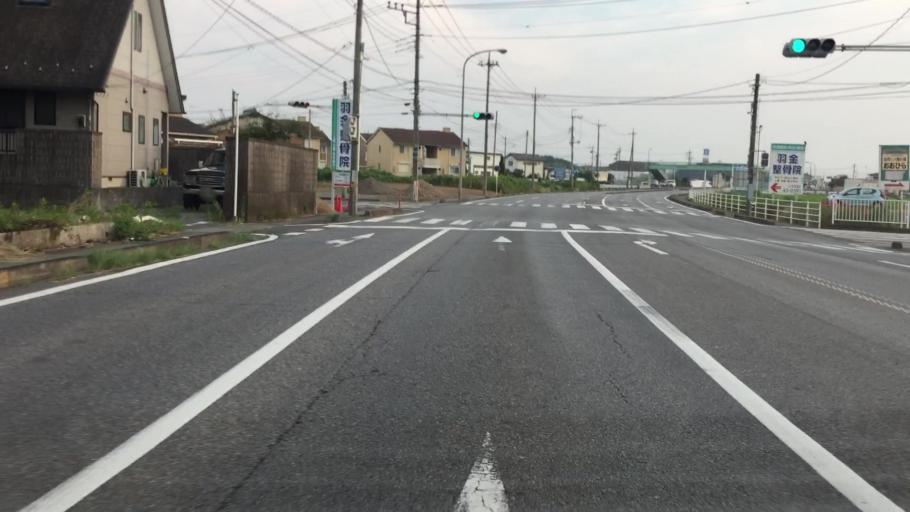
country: JP
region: Tochigi
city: Tochigi
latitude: 36.3330
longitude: 139.6939
